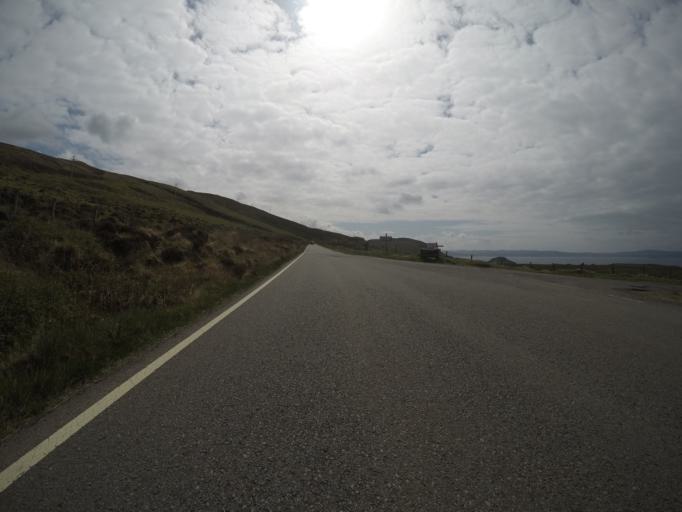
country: GB
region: Scotland
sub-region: Highland
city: Portree
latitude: 57.6099
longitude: -6.3737
